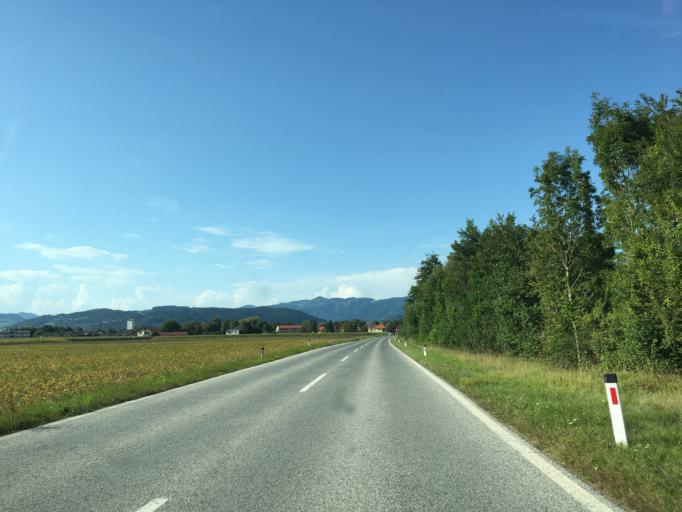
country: AT
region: Carinthia
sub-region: Politischer Bezirk Volkermarkt
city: Eberndorf
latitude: 46.6140
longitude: 14.6358
